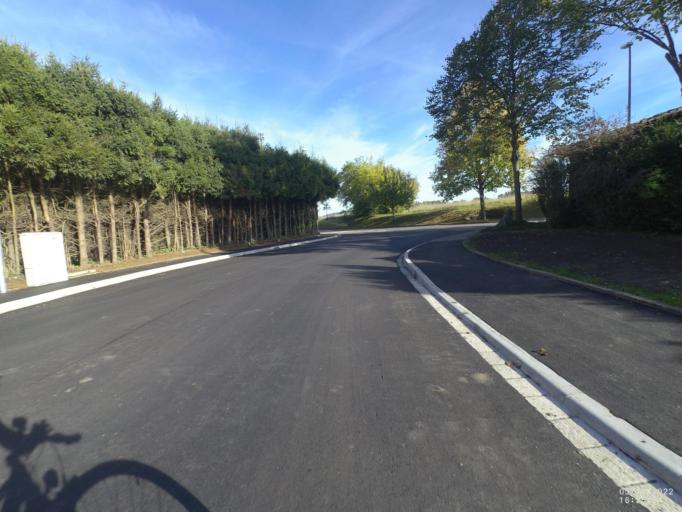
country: DE
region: Baden-Wuerttemberg
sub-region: Regierungsbezirk Stuttgart
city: Schlierbach
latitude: 48.6949
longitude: 9.5045
